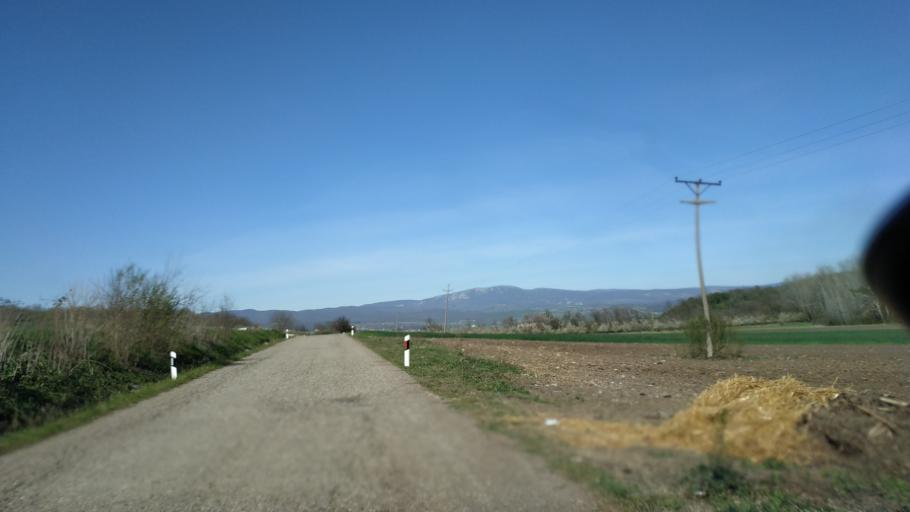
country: RS
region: Central Serbia
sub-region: Nisavski Okrug
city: Aleksinac
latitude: 43.4928
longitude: 21.6703
